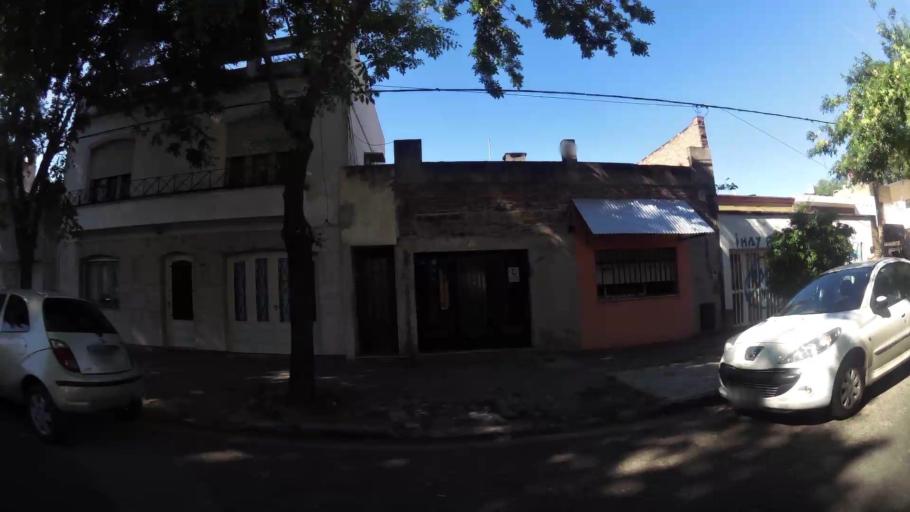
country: AR
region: Santa Fe
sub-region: Departamento de Rosario
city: Rosario
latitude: -32.9470
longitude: -60.6787
